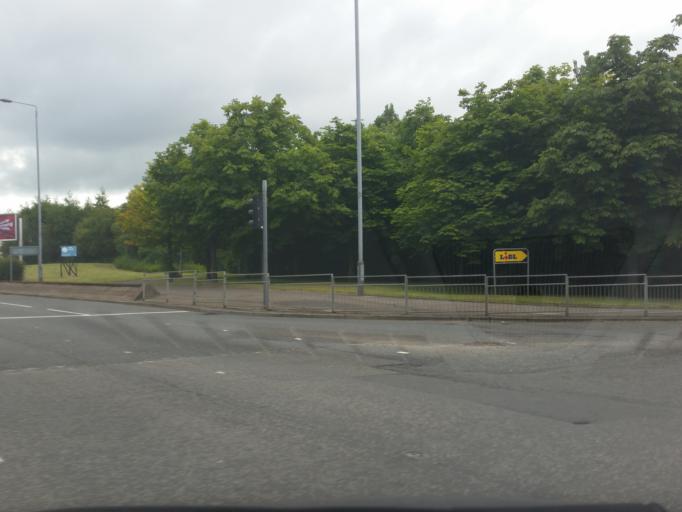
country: GB
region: Scotland
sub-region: Glasgow City
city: Glasgow
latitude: 55.8752
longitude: -4.2324
